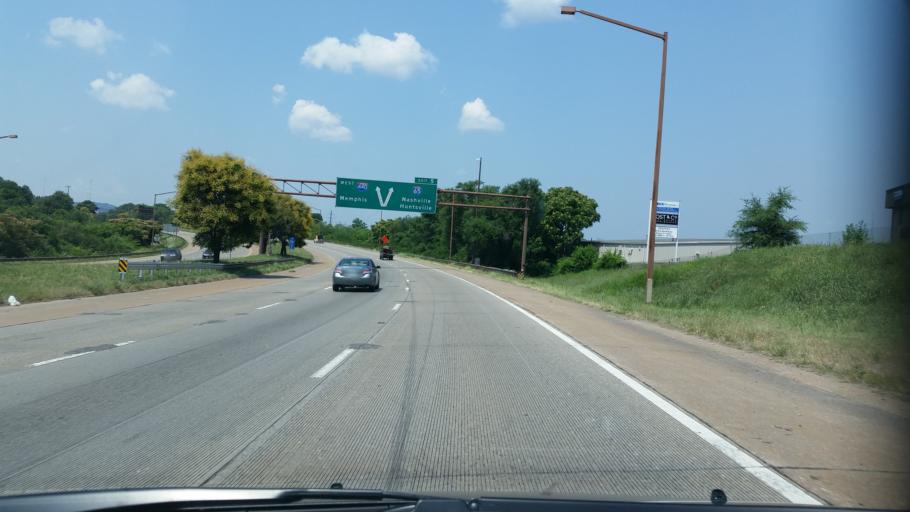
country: US
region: Tennessee
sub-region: Davidson County
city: Oak Hill
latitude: 36.1220
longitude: -86.7622
